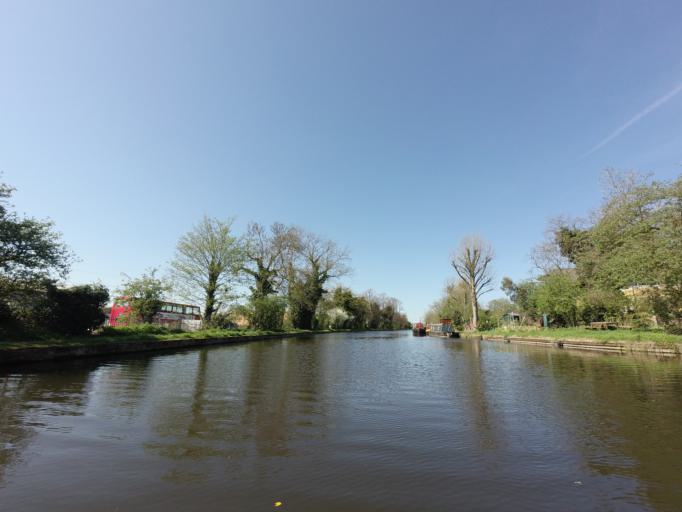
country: GB
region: England
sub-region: Greater London
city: Uxbridge
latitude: 51.5337
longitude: -0.4873
